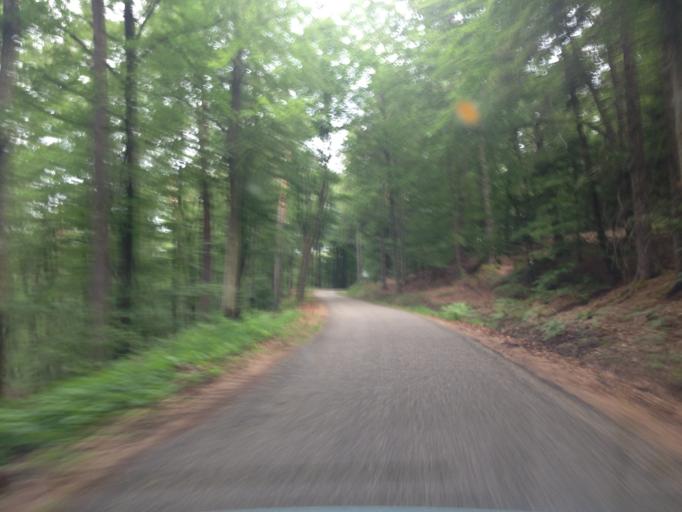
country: FR
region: Alsace
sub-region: Departement du Bas-Rhin
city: Neuwiller-les-Saverne
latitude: 48.8431
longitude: 7.3804
